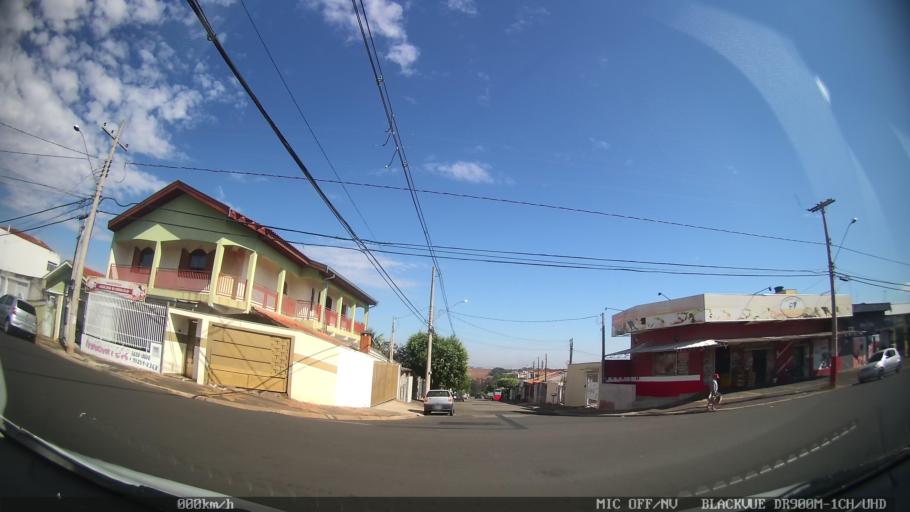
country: BR
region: Sao Paulo
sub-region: Santa Barbara D'Oeste
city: Santa Barbara d'Oeste
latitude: -22.7392
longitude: -47.3853
